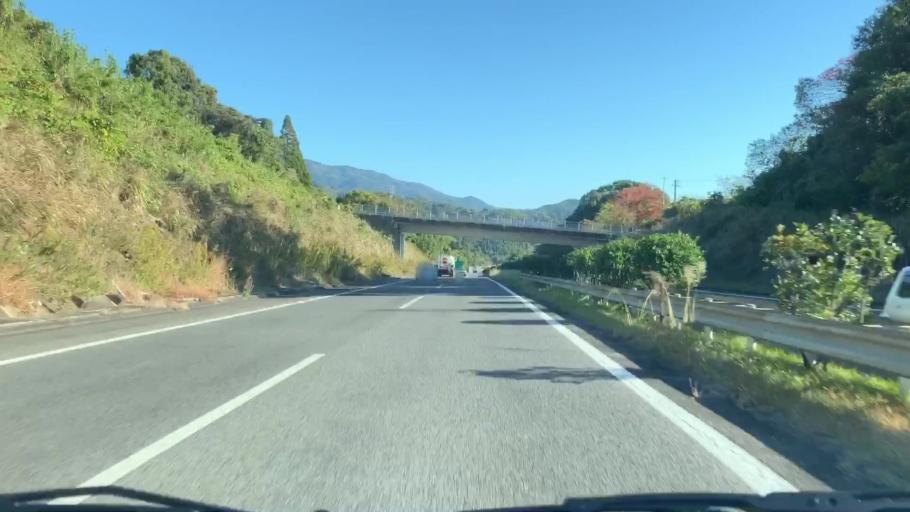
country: JP
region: Saga Prefecture
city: Saga-shi
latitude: 33.2914
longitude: 130.1661
